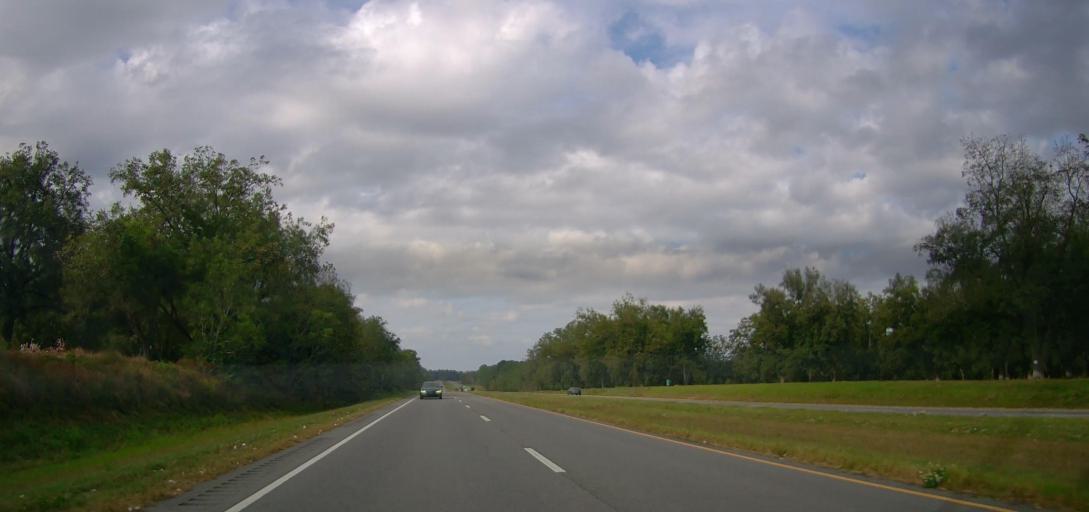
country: US
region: Georgia
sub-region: Thomas County
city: Meigs
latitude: 31.0355
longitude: -84.0650
